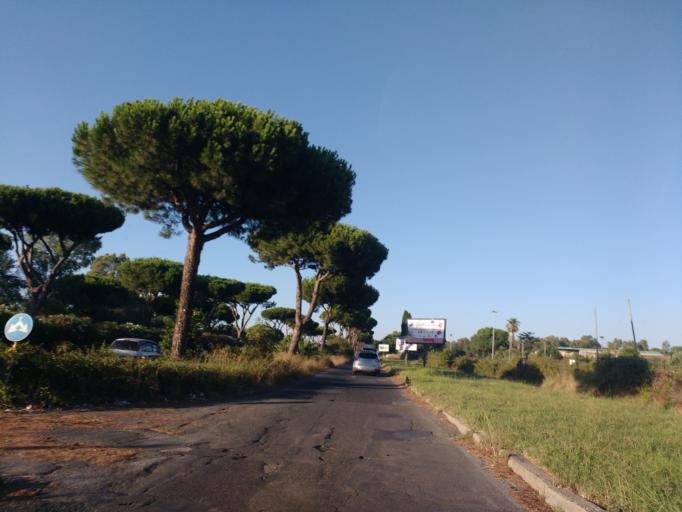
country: IT
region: Latium
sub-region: Citta metropolitana di Roma Capitale
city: Acilia-Castel Fusano-Ostia Antica
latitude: 41.7559
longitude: 12.3714
